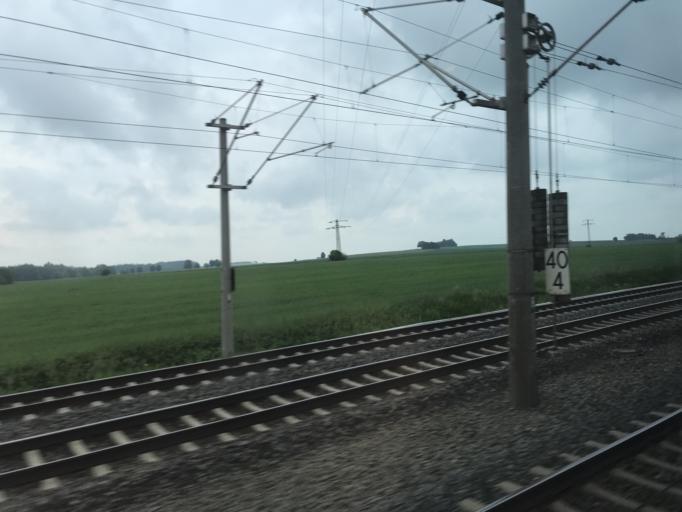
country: DE
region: Bavaria
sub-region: Upper Bavaria
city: Althegnenberg
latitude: 48.2390
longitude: 11.0567
